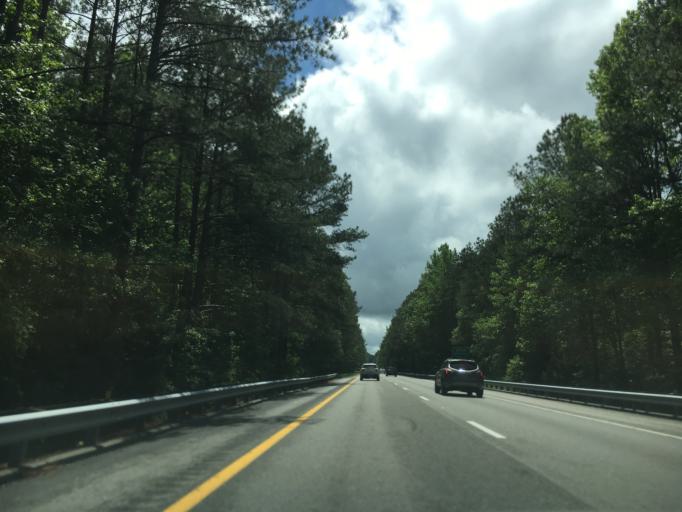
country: US
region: Virginia
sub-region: Brunswick County
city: Lawrenceville
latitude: 36.8154
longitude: -77.9710
